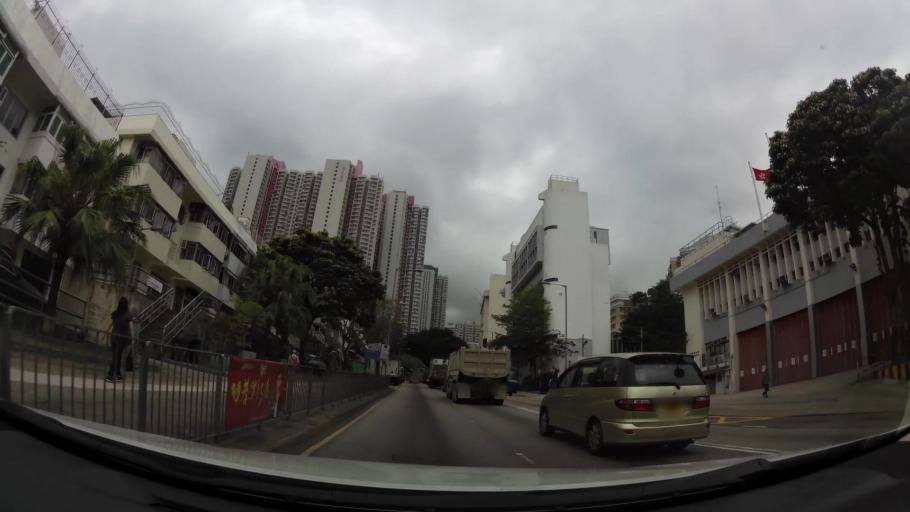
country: HK
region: Tsuen Wan
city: Tsuen Wan
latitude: 22.3746
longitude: 114.1364
